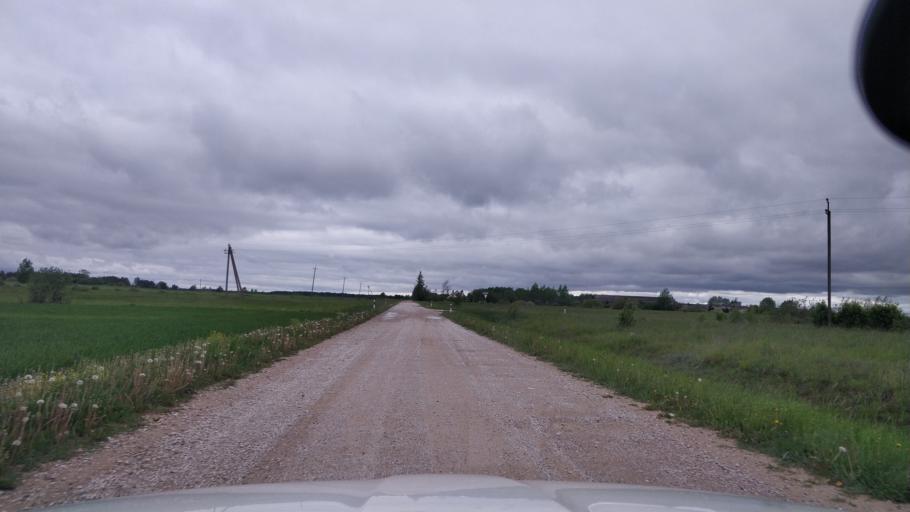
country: EE
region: Raplamaa
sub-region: Maerjamaa vald
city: Marjamaa
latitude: 58.7148
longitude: 24.2429
